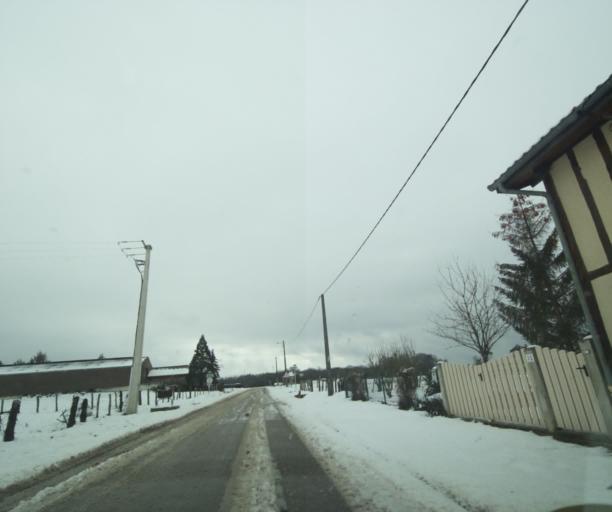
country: FR
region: Champagne-Ardenne
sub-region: Departement de la Haute-Marne
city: Montier-en-Der
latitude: 48.4311
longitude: 4.7279
